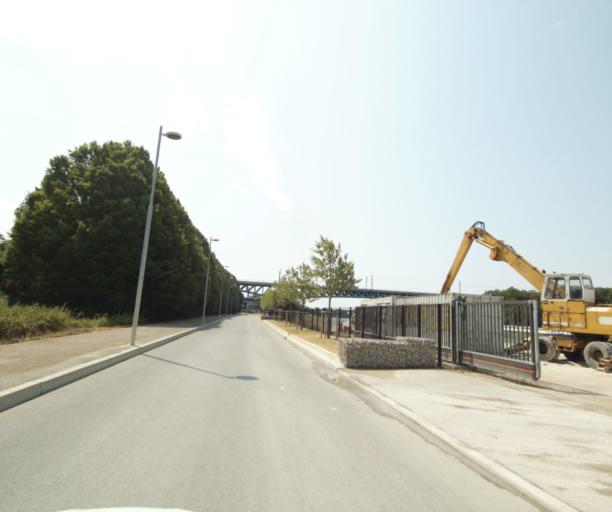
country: FR
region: Ile-de-France
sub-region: Departement des Yvelines
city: Maurecourt
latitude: 48.9936
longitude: 2.0729
